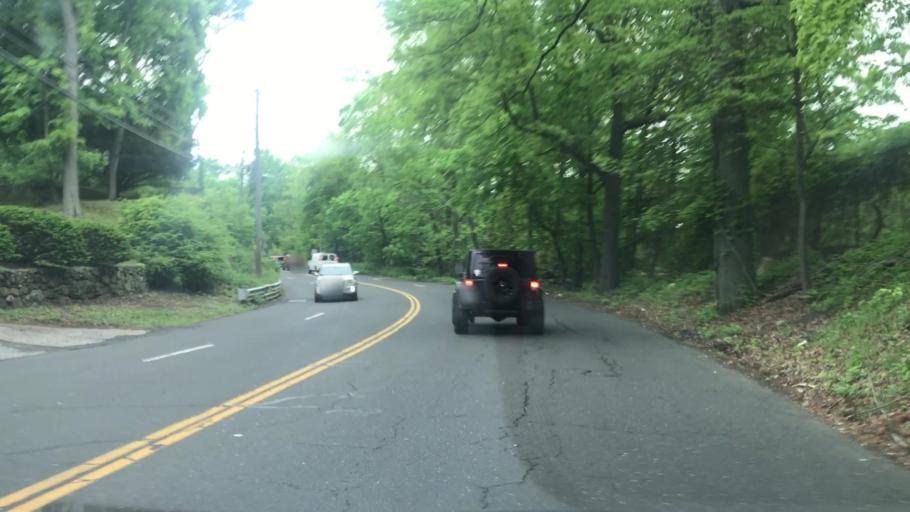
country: US
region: Connecticut
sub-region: Fairfield County
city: Stamford
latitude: 41.0630
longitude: -73.5585
